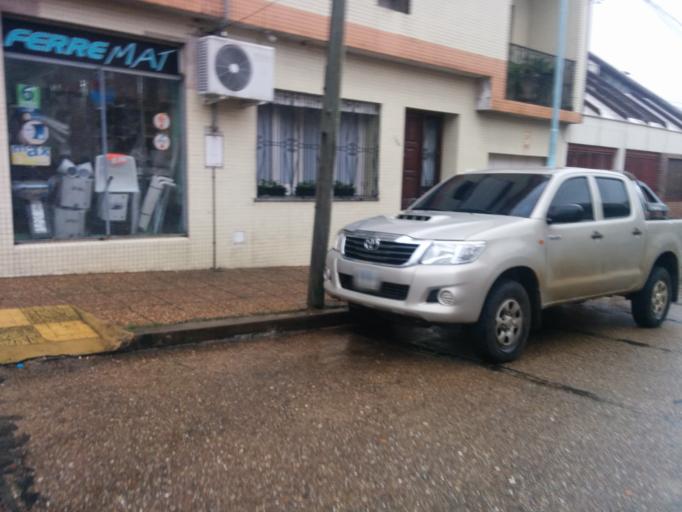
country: AR
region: Entre Rios
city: Concordia
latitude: -31.3891
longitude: -58.0148
